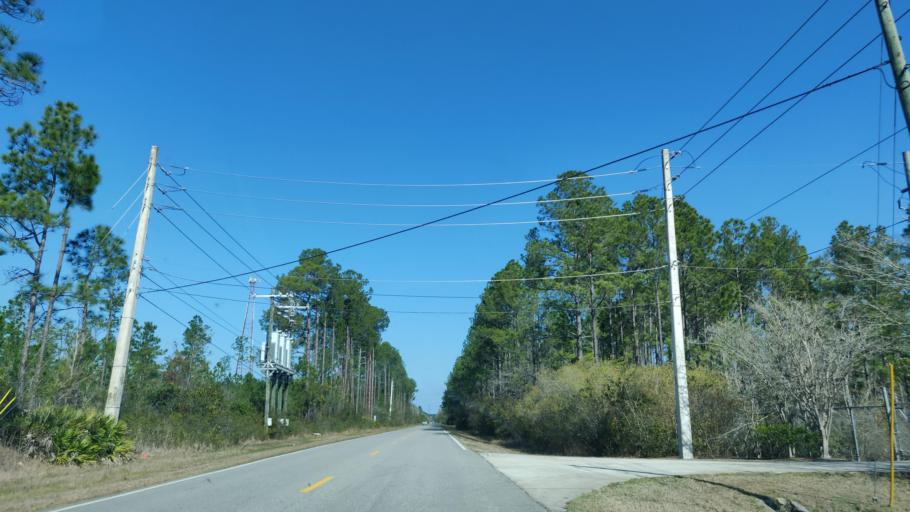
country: US
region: Florida
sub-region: Duval County
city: Baldwin
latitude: 30.2703
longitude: -81.9584
